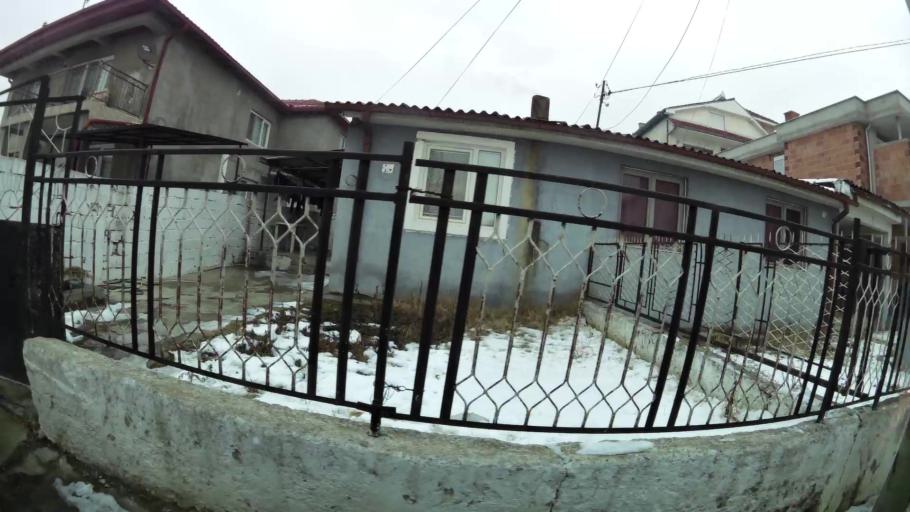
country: MK
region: Suto Orizari
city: Suto Orizare
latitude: 42.0462
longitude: 21.4214
